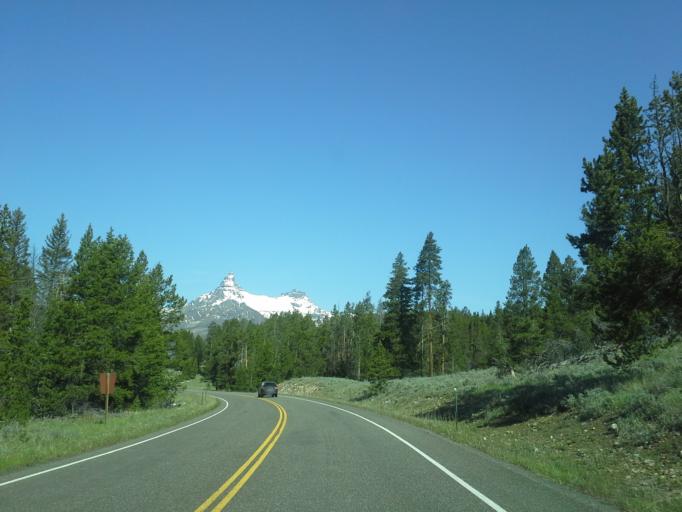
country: US
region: Montana
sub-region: Carbon County
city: Red Lodge
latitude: 44.9437
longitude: -109.7756
